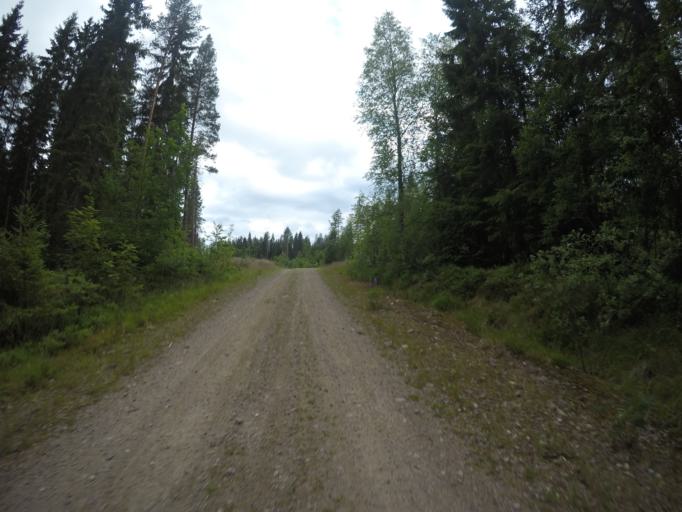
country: SE
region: Vaermland
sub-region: Filipstads Kommun
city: Lesjofors
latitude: 60.1487
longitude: 14.3906
